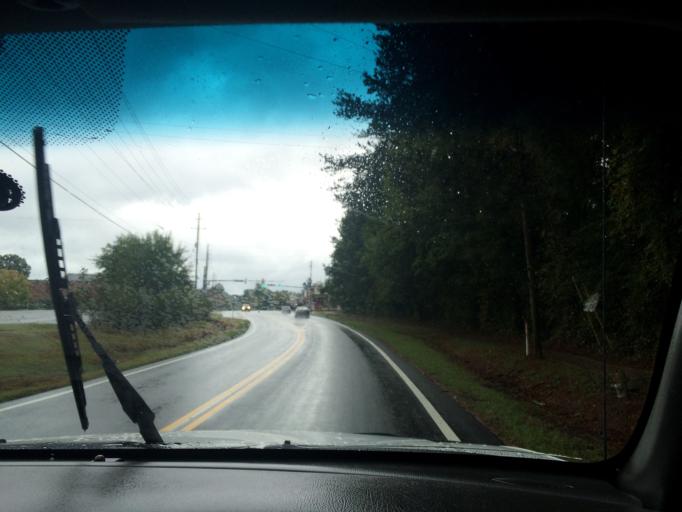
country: US
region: Georgia
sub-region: Cobb County
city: Acworth
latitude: 34.0399
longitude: -84.6523
